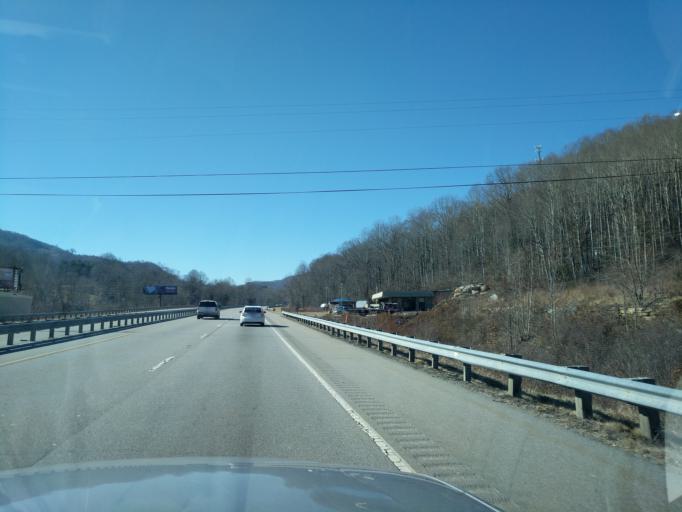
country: US
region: North Carolina
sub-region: Haywood County
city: Hazelwood
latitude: 35.4578
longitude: -83.0302
